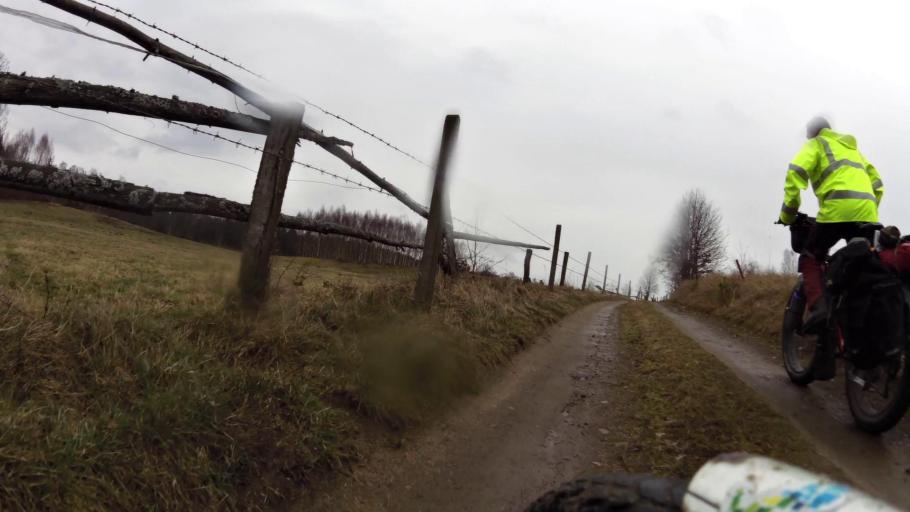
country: PL
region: Pomeranian Voivodeship
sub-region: Powiat bytowski
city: Miastko
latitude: 54.0275
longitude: 17.0234
